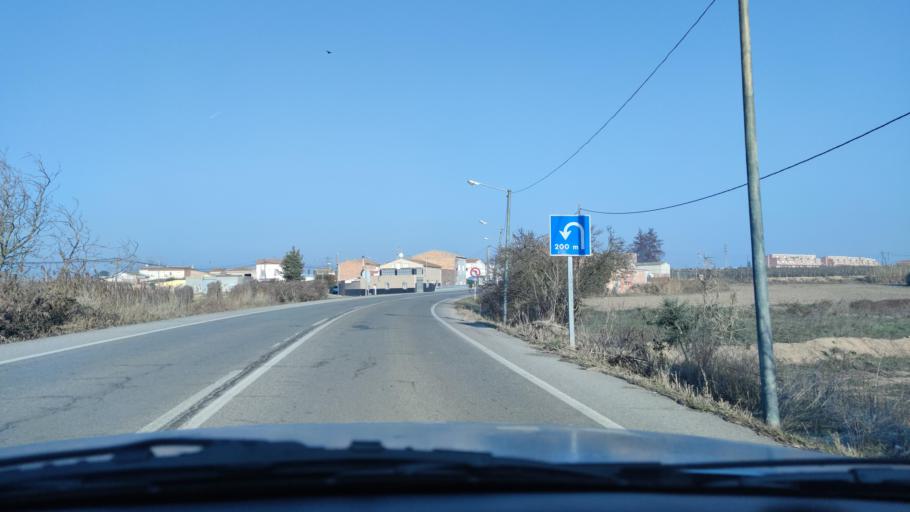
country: ES
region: Catalonia
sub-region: Provincia de Lleida
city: Lleida
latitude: 41.6423
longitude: 0.6356
